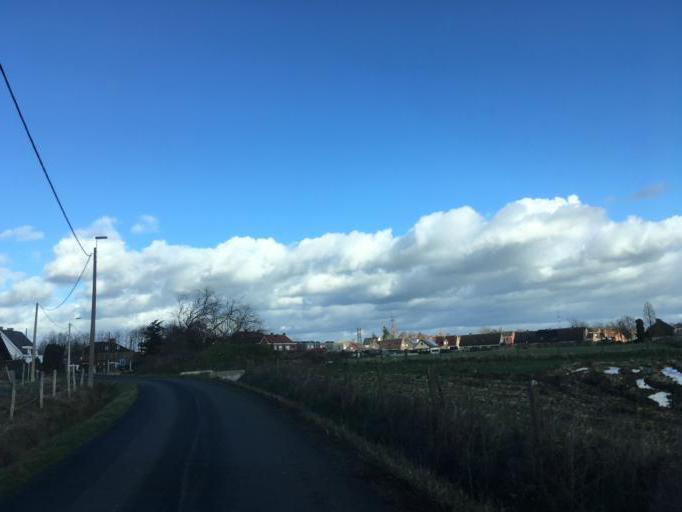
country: BE
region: Flanders
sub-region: Provincie West-Vlaanderen
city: Ardooie
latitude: 50.9556
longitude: 3.1649
